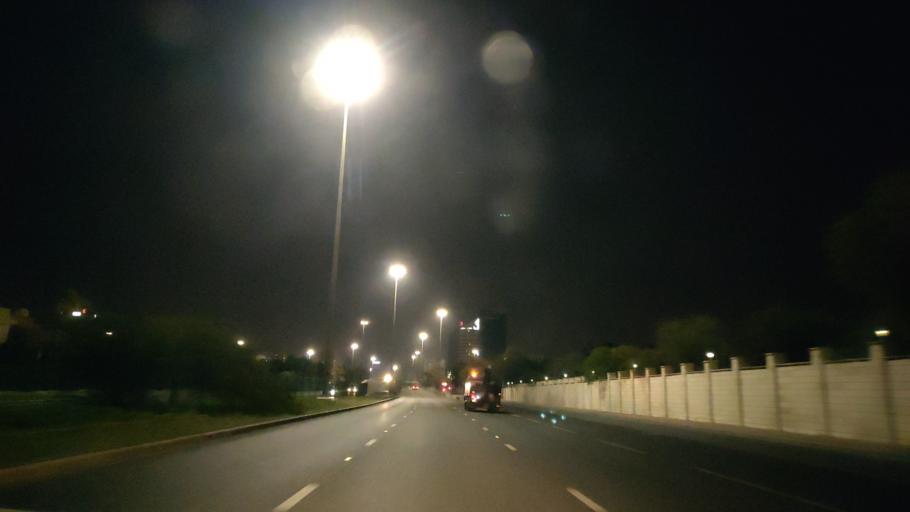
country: KW
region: Muhafazat Hawalli
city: Hawalli
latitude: 29.3220
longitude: 48.0068
